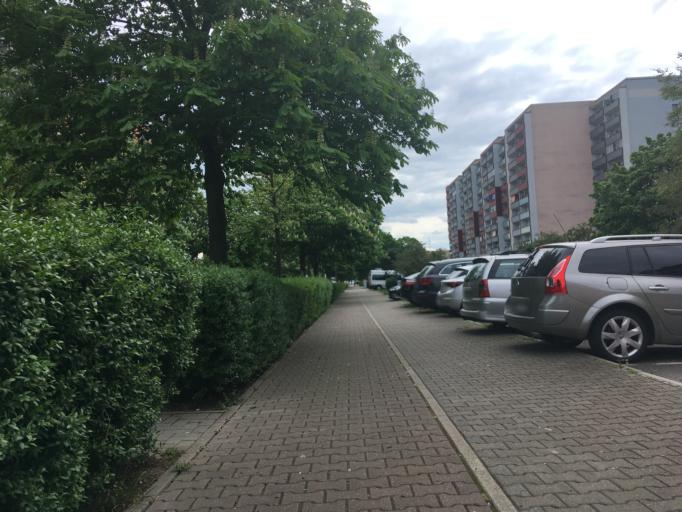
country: DE
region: Berlin
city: Hellersdorf
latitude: 52.5473
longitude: 13.5923
